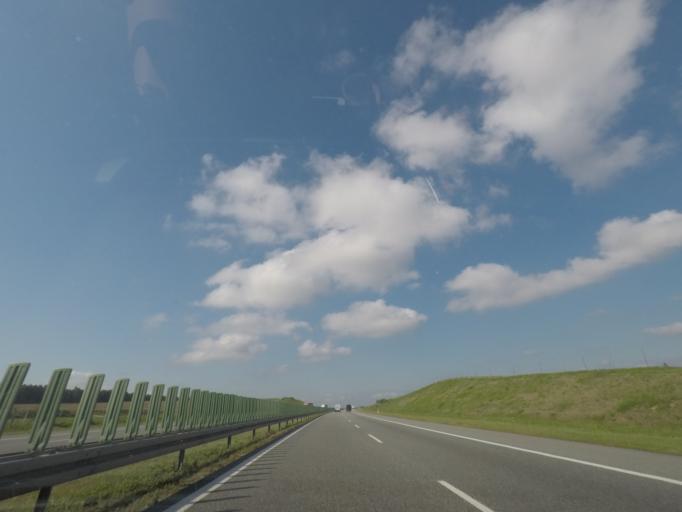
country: PL
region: Pomeranian Voivodeship
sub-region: Powiat tczewski
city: Tczew
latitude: 54.0754
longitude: 18.6848
